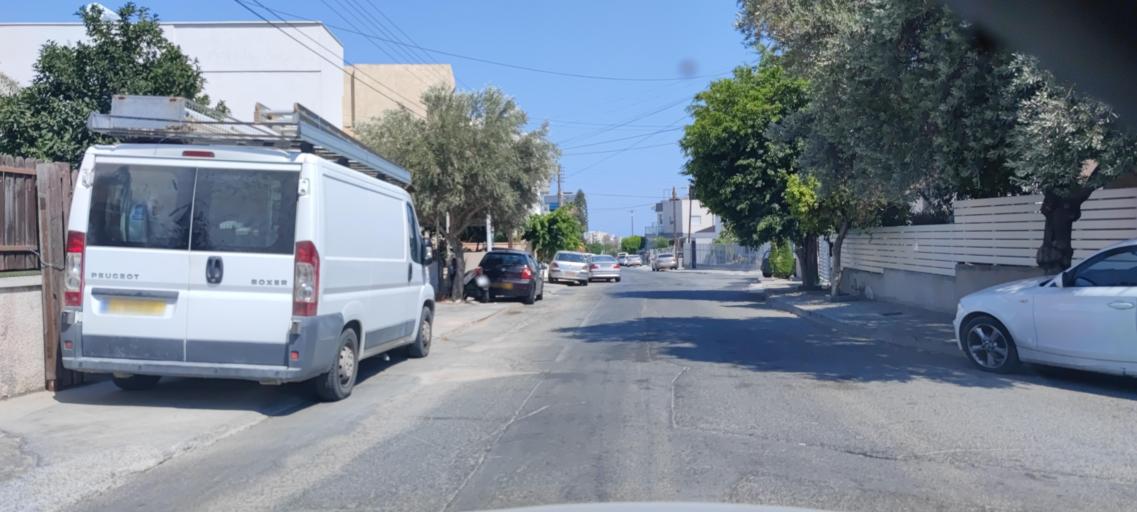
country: CY
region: Limassol
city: Limassol
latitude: 34.6996
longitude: 33.0519
